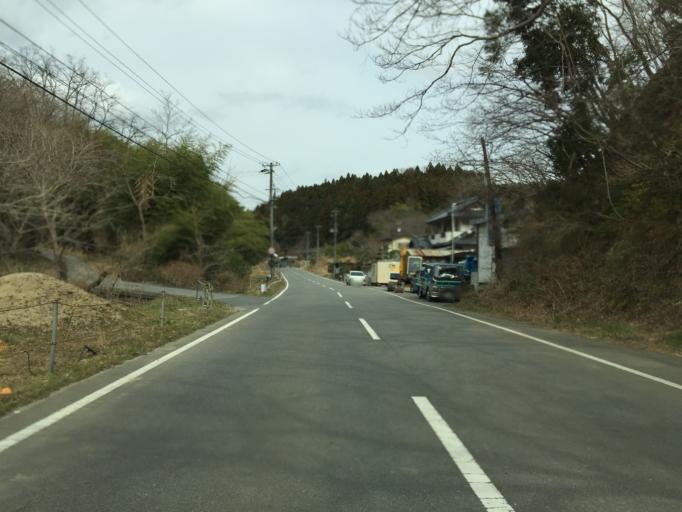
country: JP
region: Fukushima
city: Iwaki
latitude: 37.0075
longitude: 140.8161
